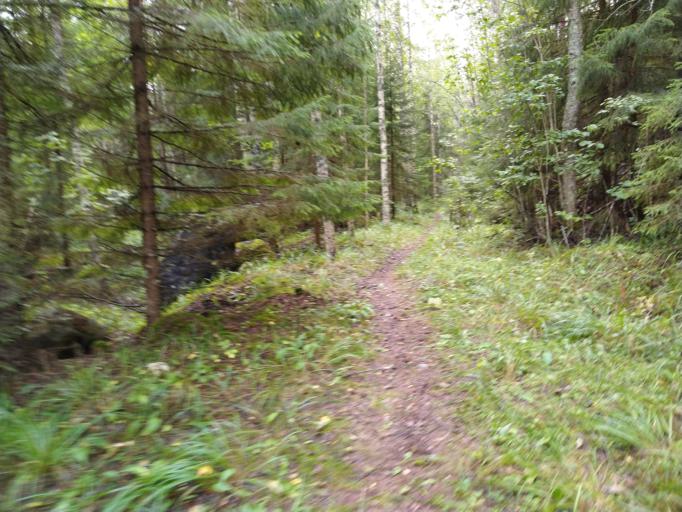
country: FI
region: Paijanne Tavastia
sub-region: Lahti
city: Auttoinen
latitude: 61.2213
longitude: 25.1682
